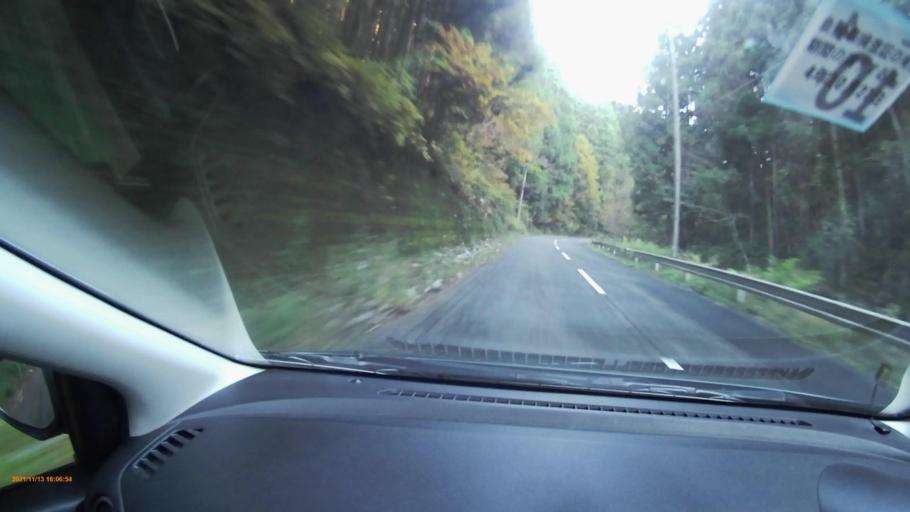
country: JP
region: Gifu
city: Nakatsugawa
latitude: 35.6028
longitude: 137.4773
